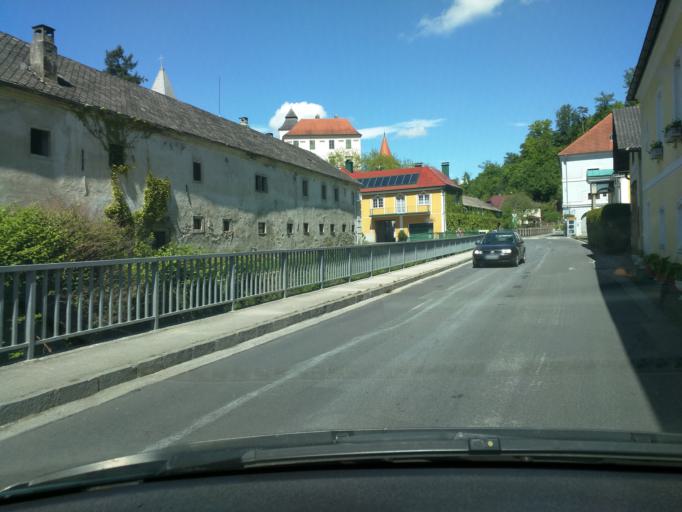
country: AT
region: Lower Austria
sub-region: Politischer Bezirk Amstetten
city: Sankt Georgen am Ybbsfelde
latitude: 48.1355
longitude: 14.9214
